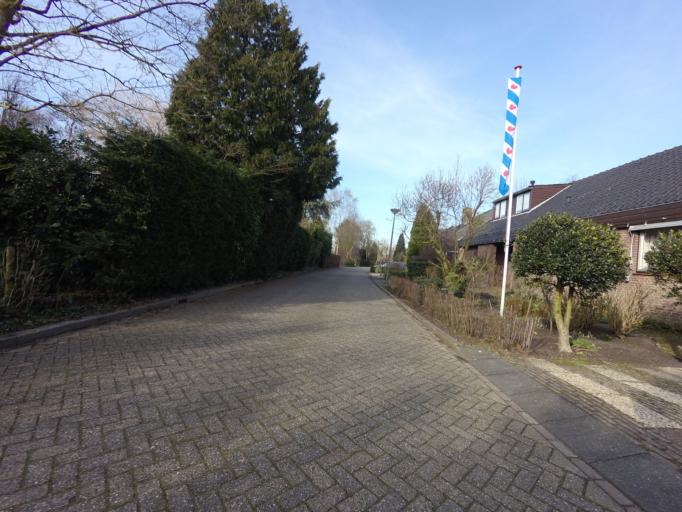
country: NL
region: South Holland
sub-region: Gemeente Hardinxveld-Giessendam
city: Neder-Hardinxveld
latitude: 51.8382
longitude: 4.8685
